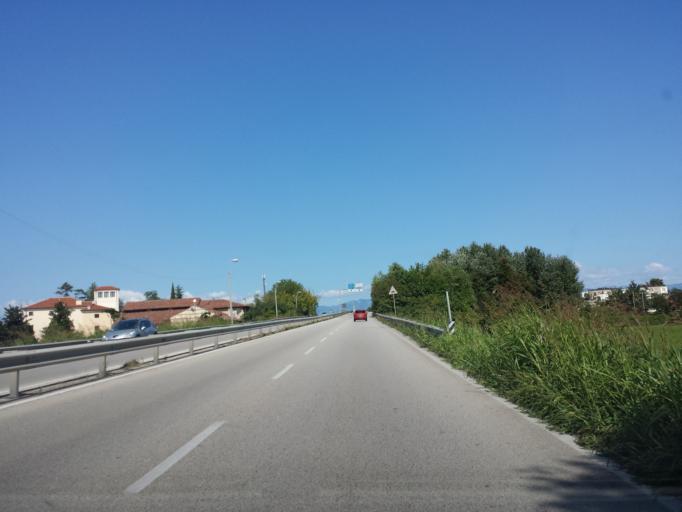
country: IT
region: Veneto
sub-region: Provincia di Vicenza
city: Villaggio Montegrappa
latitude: 45.5354
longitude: 11.5893
